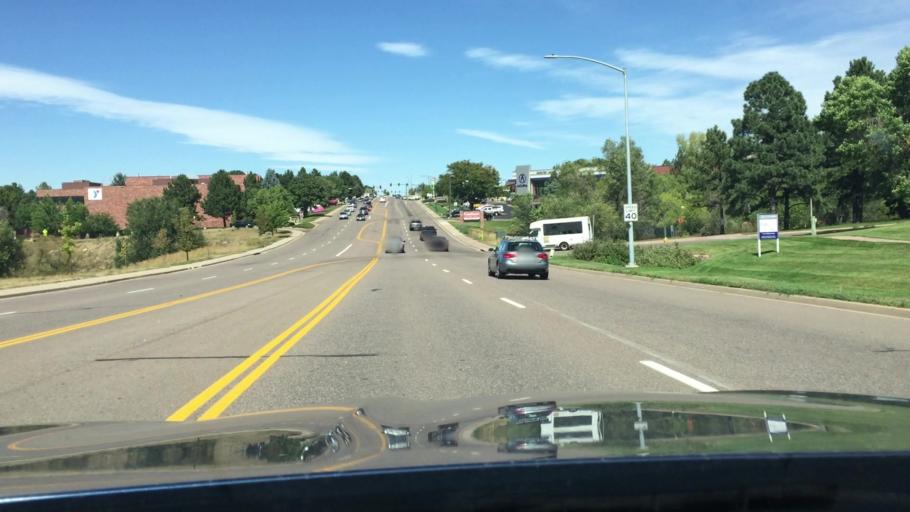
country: US
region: Colorado
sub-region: Douglas County
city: Highlands Ranch
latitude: 39.5773
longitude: -104.9884
